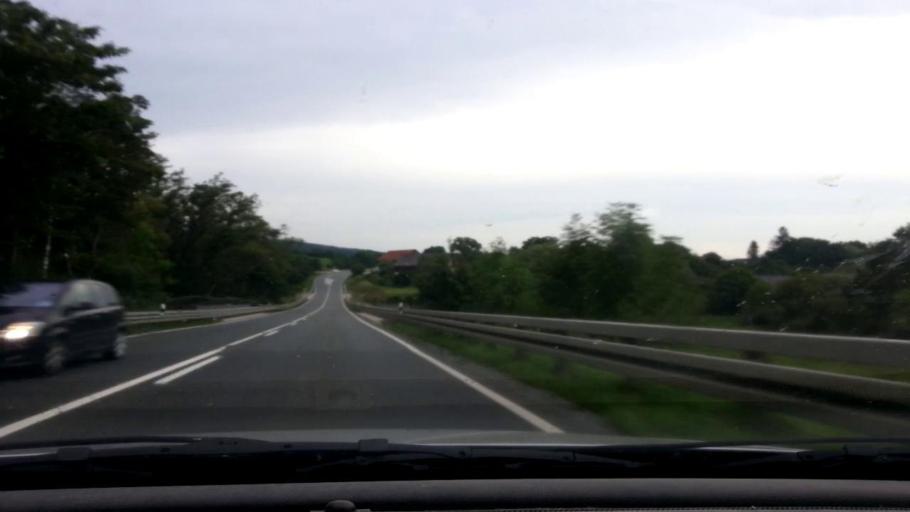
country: DE
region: Bavaria
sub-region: Upper Franconia
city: Emtmannsberg
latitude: 49.9090
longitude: 11.6670
